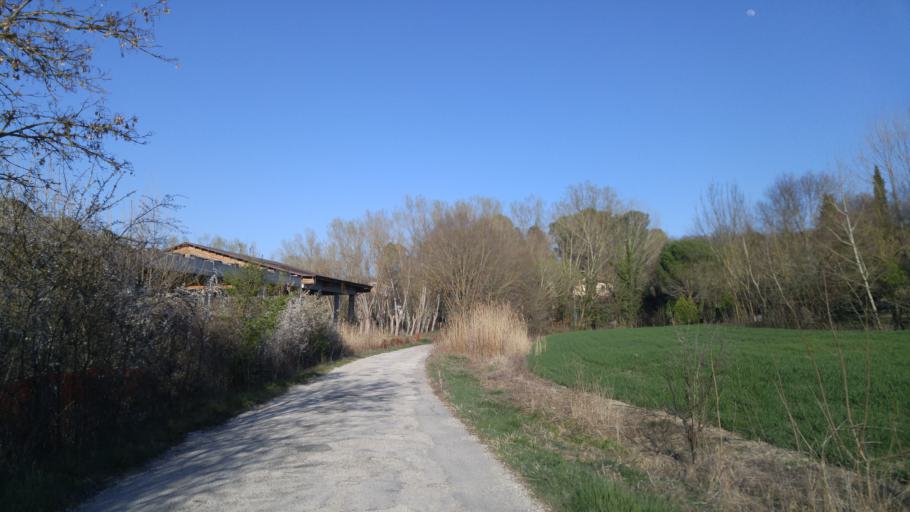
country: IT
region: The Marches
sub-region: Provincia di Pesaro e Urbino
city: Fenile
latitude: 43.8268
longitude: 12.9164
